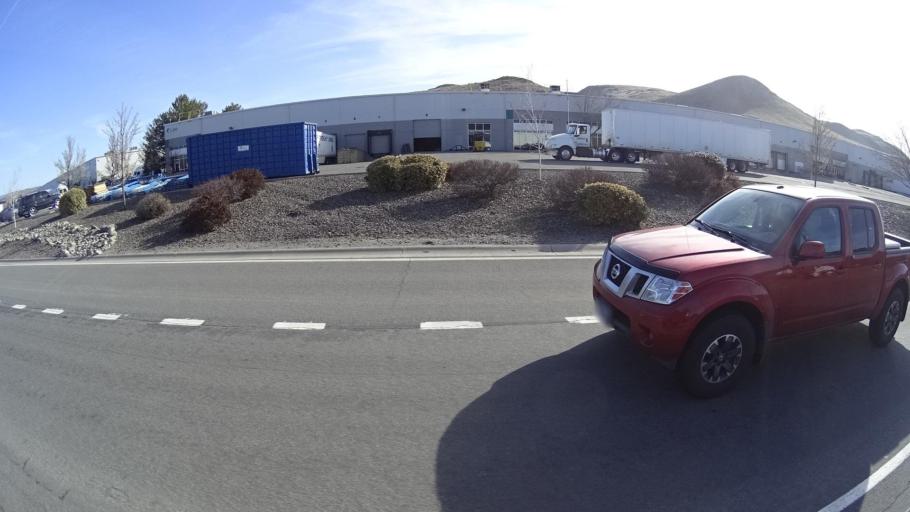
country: US
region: Nevada
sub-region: Washoe County
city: Sparks
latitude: 39.5314
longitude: -119.7035
